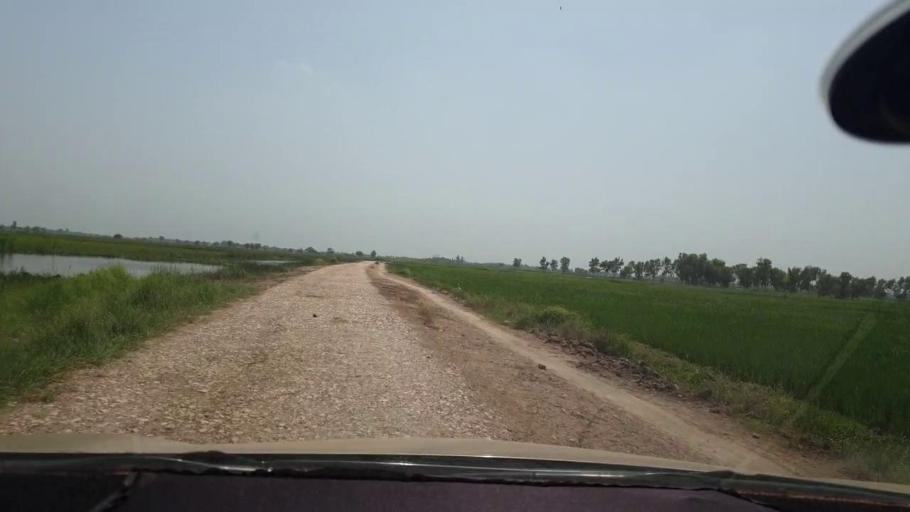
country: PK
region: Sindh
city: Kambar
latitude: 27.6528
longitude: 67.9315
